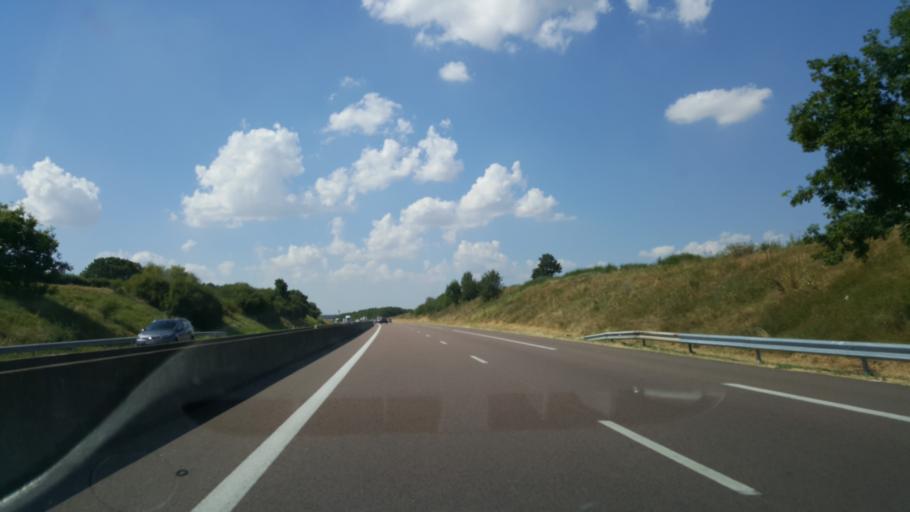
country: FR
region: Bourgogne
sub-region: Departement de la Cote-d'Or
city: Vitteaux
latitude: 47.3464
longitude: 4.4592
